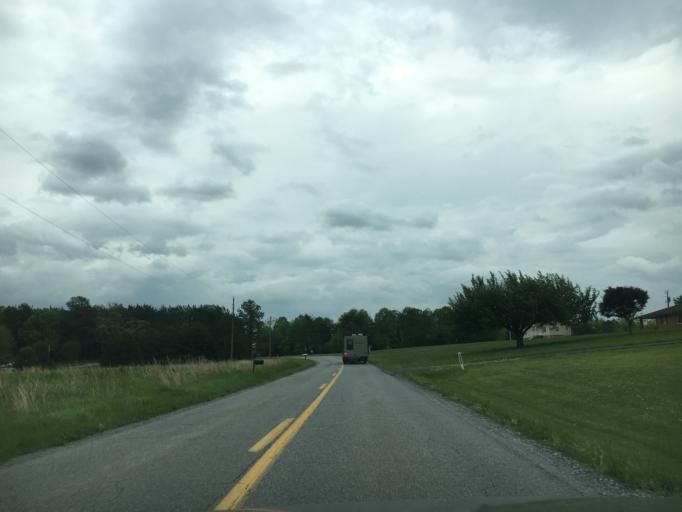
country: US
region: Virginia
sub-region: Campbell County
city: Rustburg
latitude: 37.2162
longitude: -79.0424
